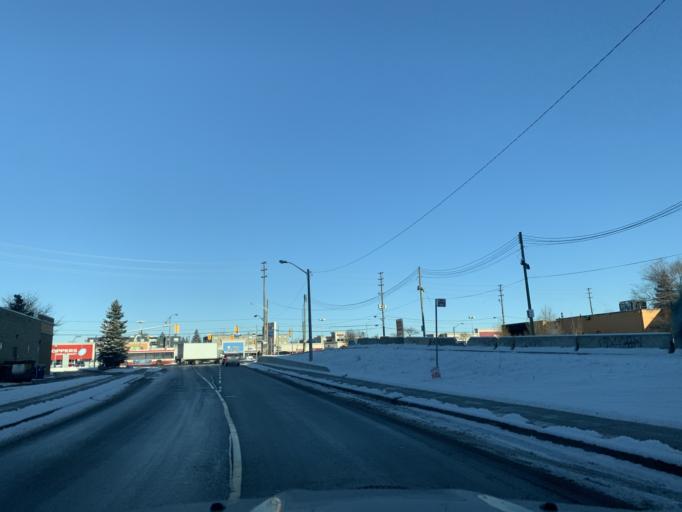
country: CA
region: Ontario
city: Toronto
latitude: 43.7267
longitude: -79.4800
